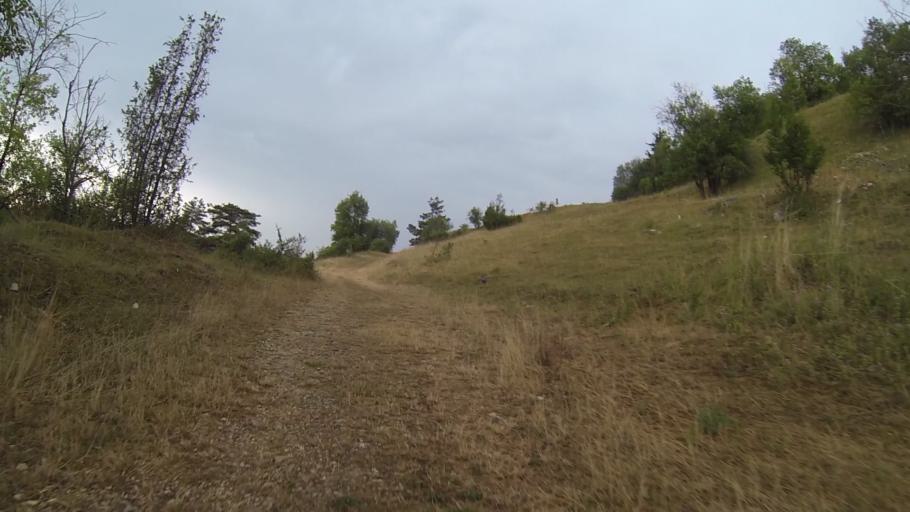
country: DE
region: Baden-Wuerttemberg
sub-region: Regierungsbezirk Stuttgart
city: Heidenheim an der Brenz
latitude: 48.6989
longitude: 10.1763
